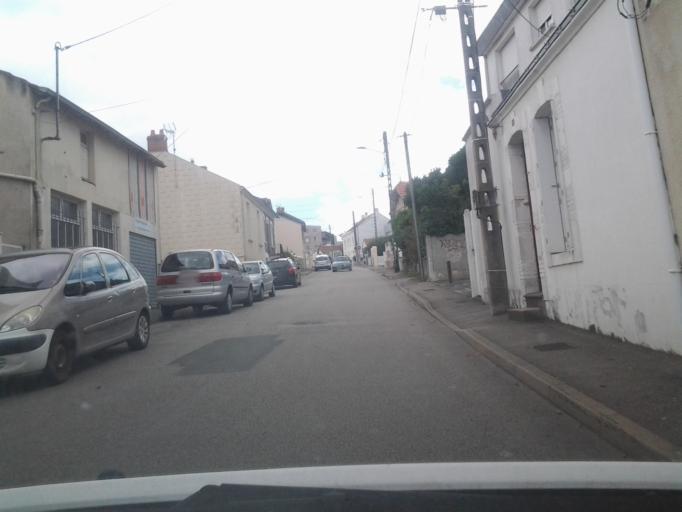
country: FR
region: Pays de la Loire
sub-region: Departement de la Vendee
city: La Roche-sur-Yon
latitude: 46.6631
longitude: -1.4313
